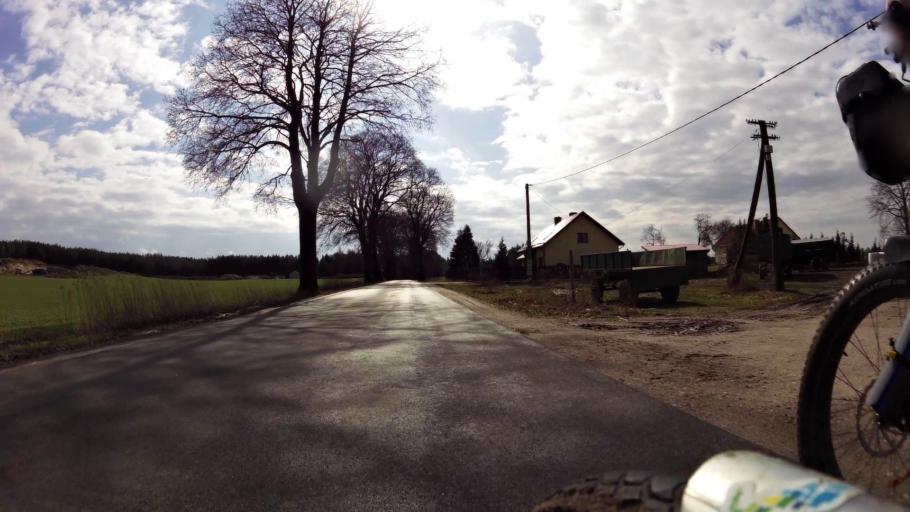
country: PL
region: Pomeranian Voivodeship
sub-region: Powiat bytowski
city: Kolczyglowy
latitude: 54.2097
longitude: 17.2352
